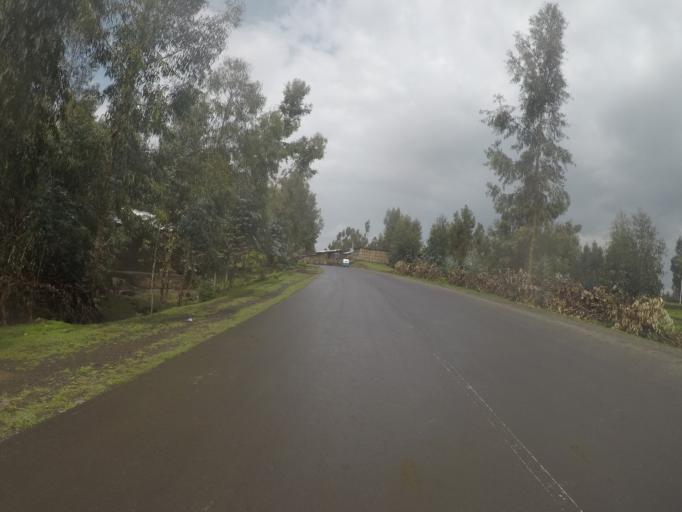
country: ET
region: Amhara
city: Debark'
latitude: 13.1180
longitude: 37.8793
